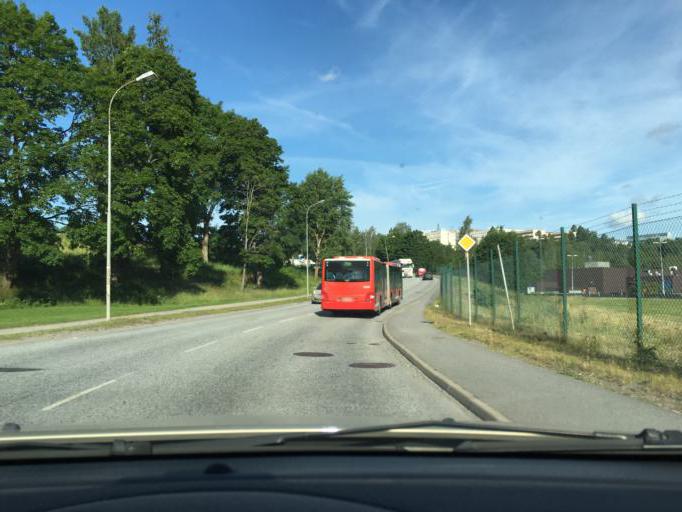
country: SE
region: Stockholm
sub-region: Sodertalje Kommun
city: Pershagen
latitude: 59.1652
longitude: 17.6445
